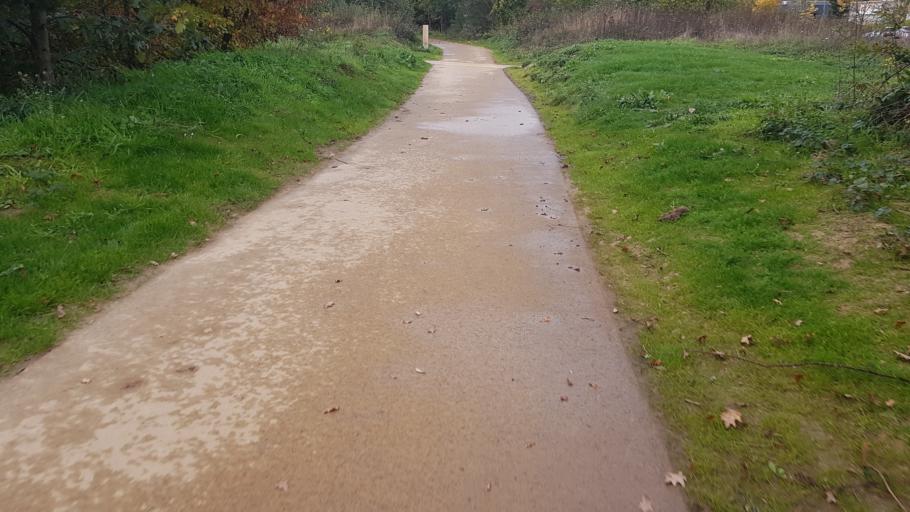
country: BE
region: Flanders
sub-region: Provincie Vlaams-Brabant
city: Wemmel
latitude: 50.8794
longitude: 4.2949
